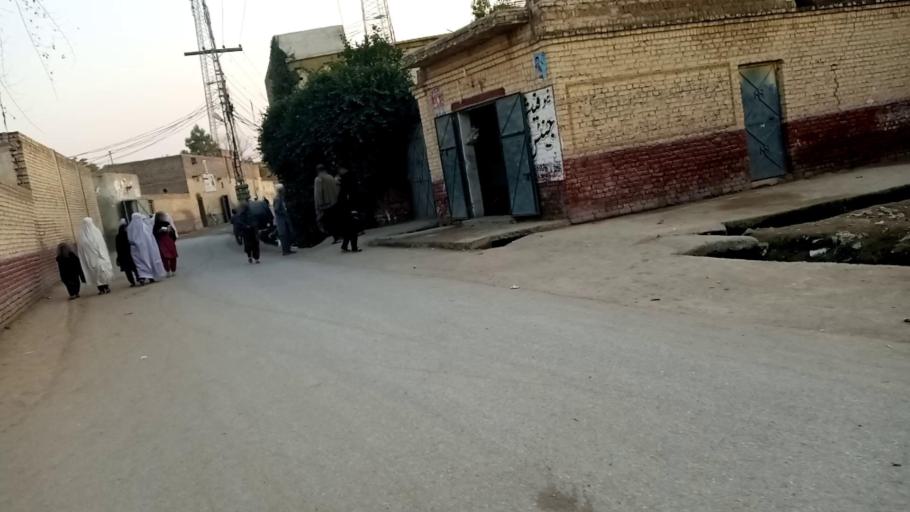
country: PK
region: Khyber Pakhtunkhwa
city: Peshawar
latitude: 34.0505
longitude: 71.4597
